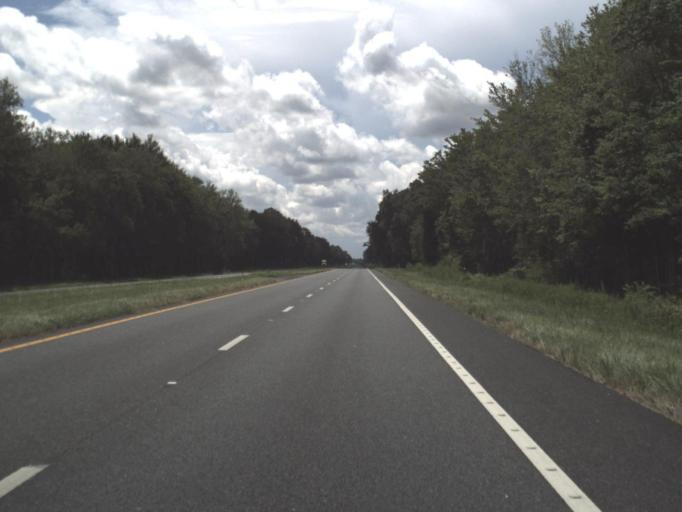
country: US
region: Florida
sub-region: Taylor County
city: Perry
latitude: 30.2146
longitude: -83.6680
